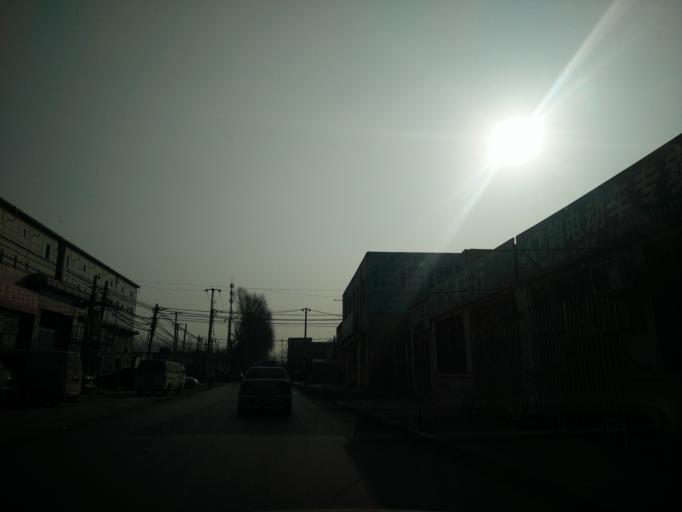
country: CN
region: Beijing
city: Xingfeng
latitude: 39.7191
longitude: 116.3757
